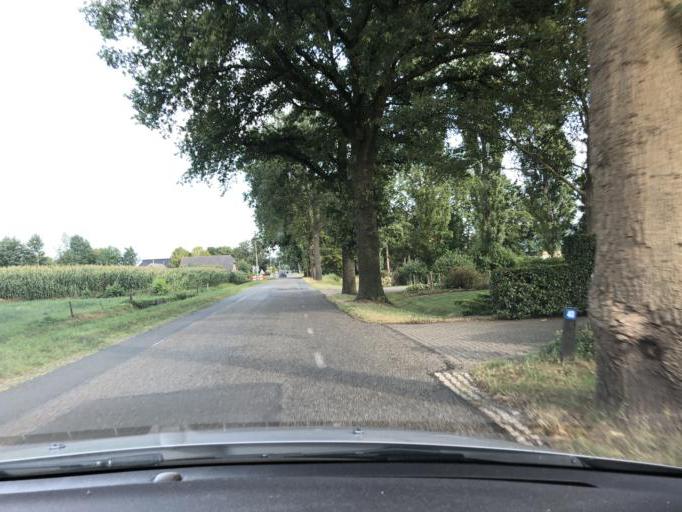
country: NL
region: Overijssel
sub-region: Gemeente Staphorst
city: Staphorst
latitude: 52.6113
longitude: 6.2677
